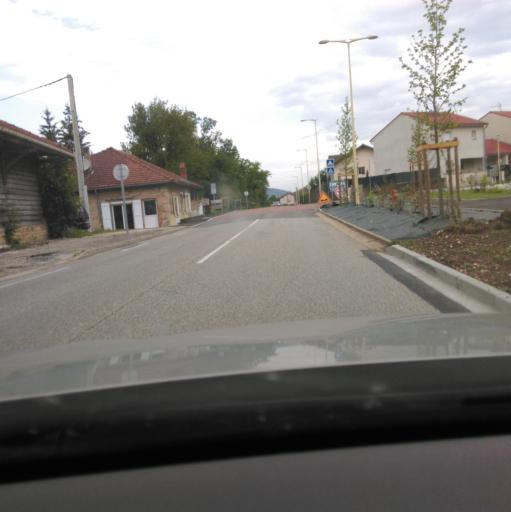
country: FR
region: Rhone-Alpes
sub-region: Departement de l'Ain
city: Izernore
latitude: 46.1887
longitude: 5.5435
